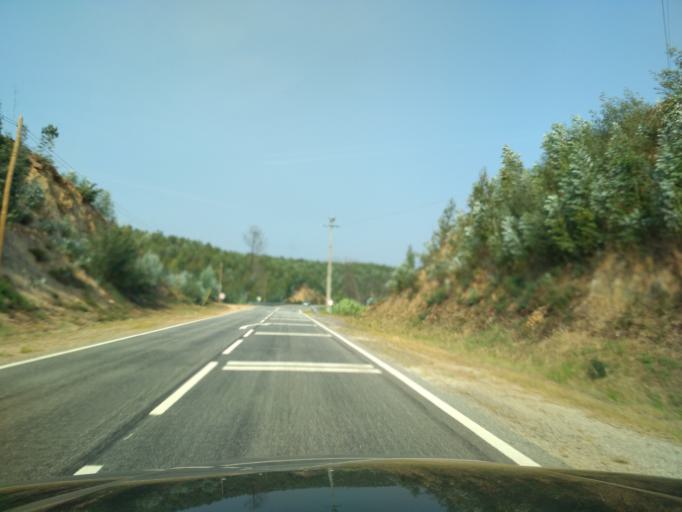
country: PT
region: Viseu
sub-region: Mortagua
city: Mortagua
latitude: 40.4036
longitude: -8.1929
